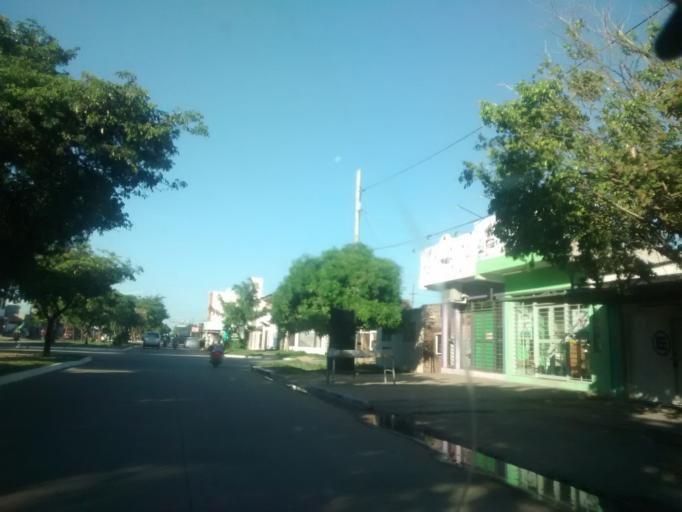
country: AR
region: Chaco
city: Resistencia
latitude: -27.4510
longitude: -59.0149
